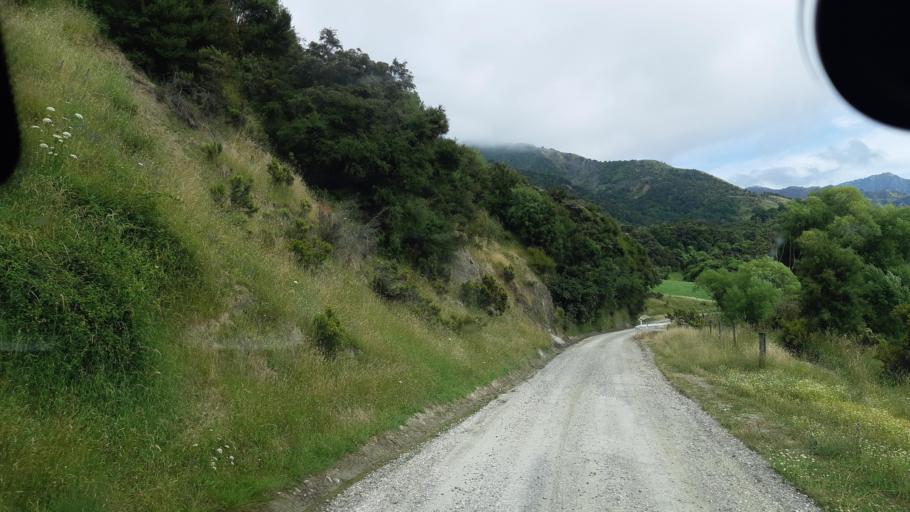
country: NZ
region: Marlborough
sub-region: Marlborough District
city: Blenheim
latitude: -41.9714
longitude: 173.9874
